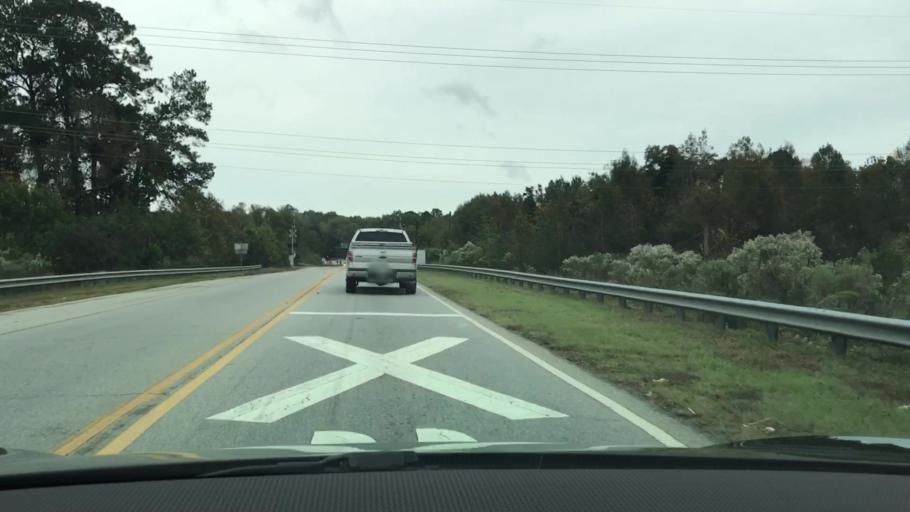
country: US
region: Georgia
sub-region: Warren County
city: West Warrenton
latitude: 33.4062
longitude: -82.6720
